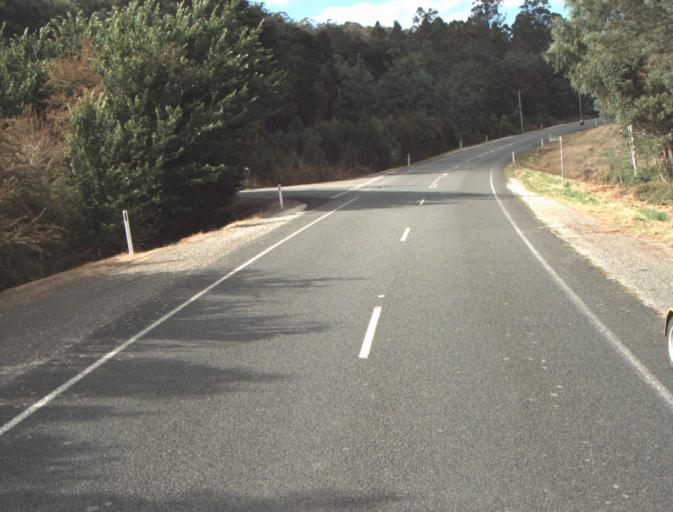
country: AU
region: Tasmania
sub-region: Launceston
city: Mayfield
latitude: -41.2785
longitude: 147.2202
